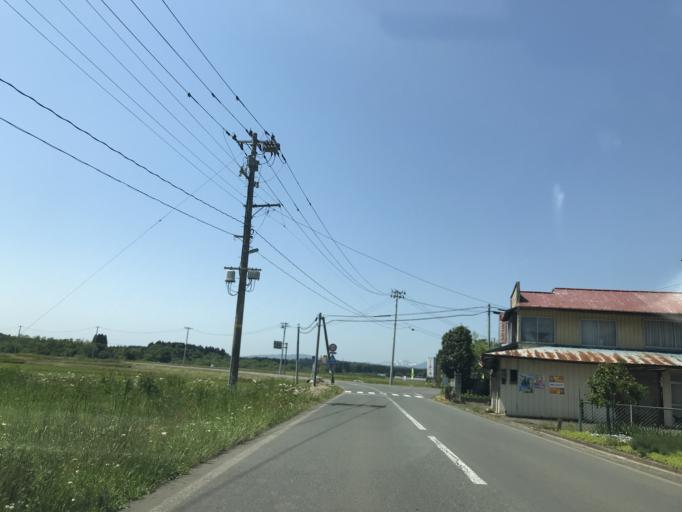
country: JP
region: Iwate
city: Mizusawa
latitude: 39.1727
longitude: 141.0614
